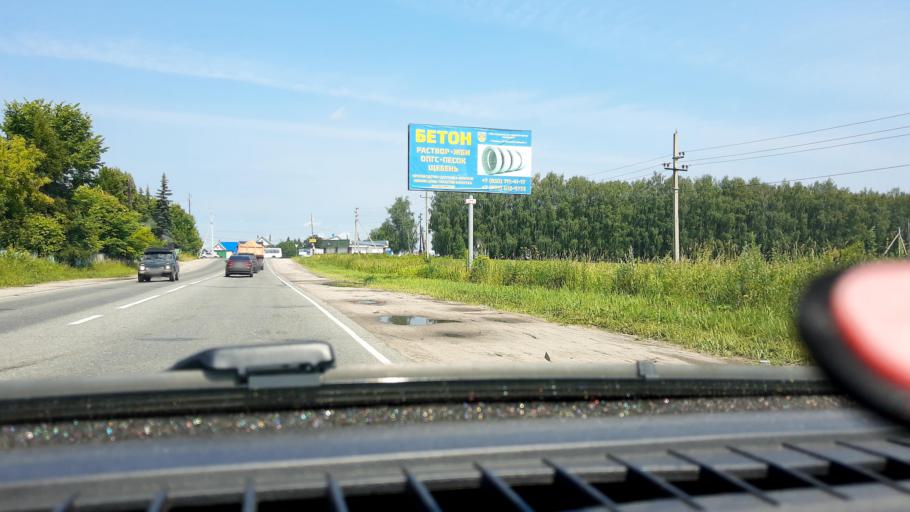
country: RU
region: Nizjnij Novgorod
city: Gorodets
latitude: 56.6442
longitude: 43.5019
